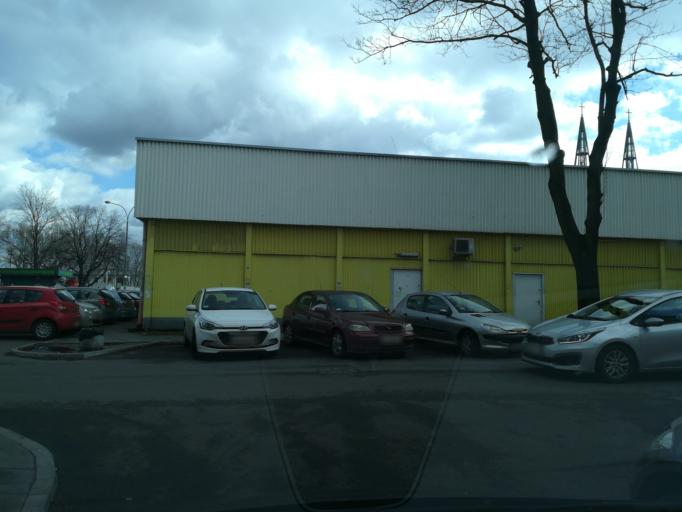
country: PL
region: Silesian Voivodeship
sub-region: Sosnowiec
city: Sosnowiec
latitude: 50.2911
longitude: 19.1312
